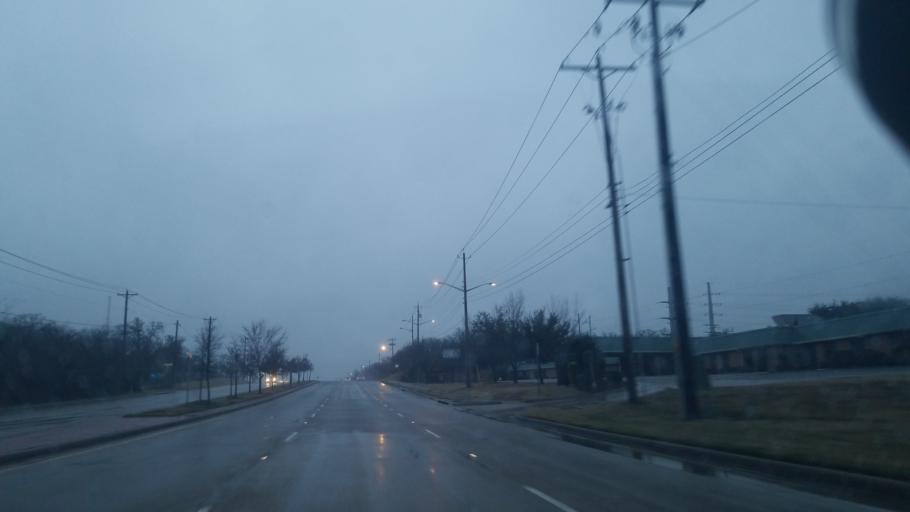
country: US
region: Texas
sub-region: Denton County
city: Denton
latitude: 33.2259
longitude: -97.0902
